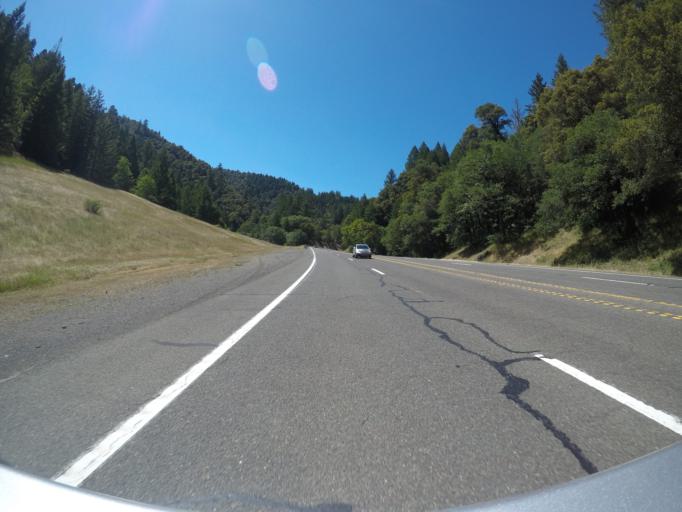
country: US
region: California
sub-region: Mendocino County
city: Laytonville
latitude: 39.5792
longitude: -123.4417
